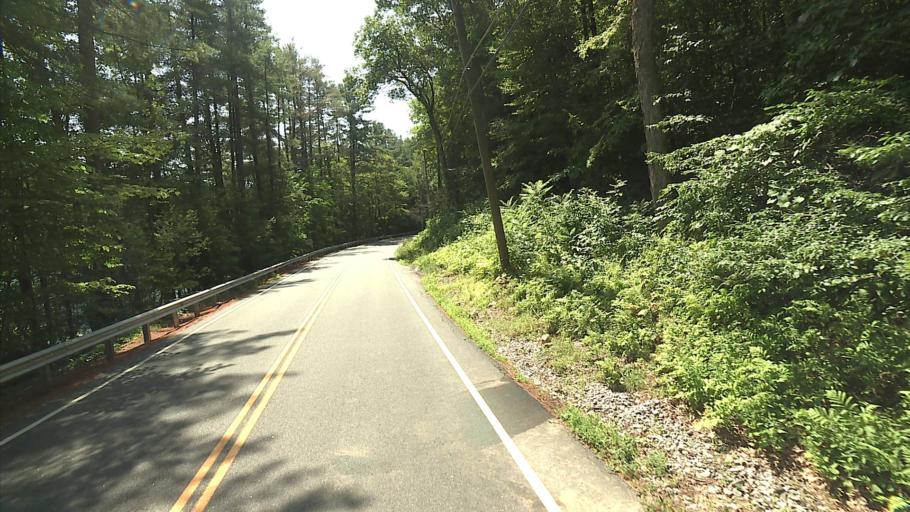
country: US
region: Connecticut
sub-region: Litchfield County
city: West Torrington
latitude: 41.8430
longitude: -73.1531
